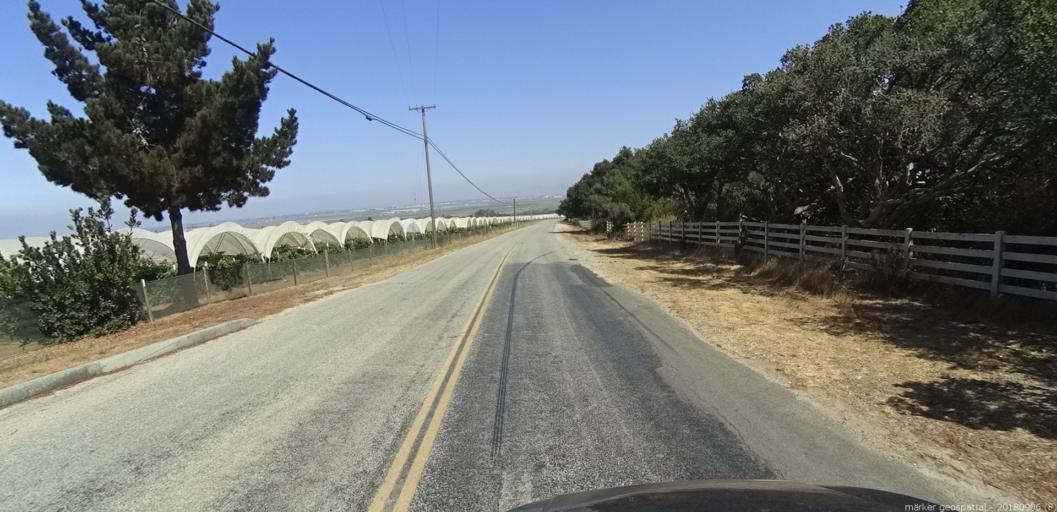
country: US
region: California
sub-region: Monterey County
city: Salinas
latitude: 36.5891
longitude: -121.6295
